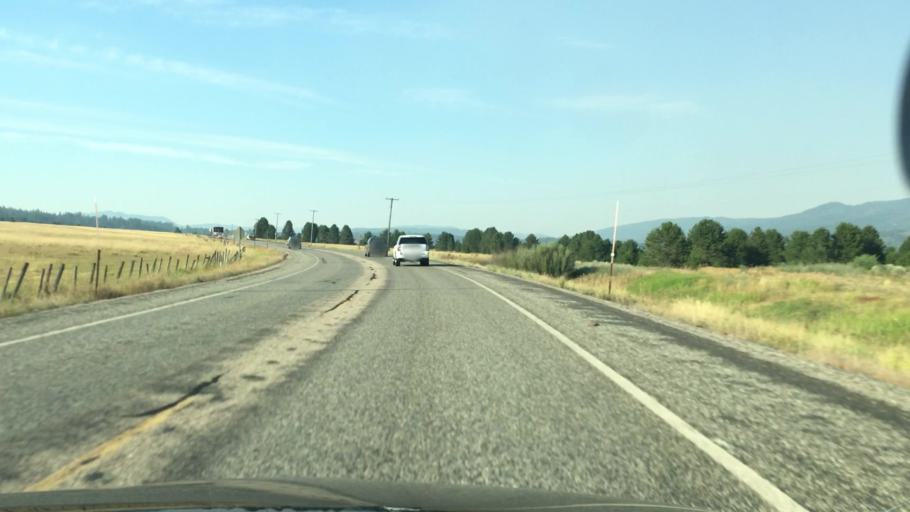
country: US
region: Idaho
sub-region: Valley County
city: Cascade
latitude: 44.3381
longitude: -116.0307
